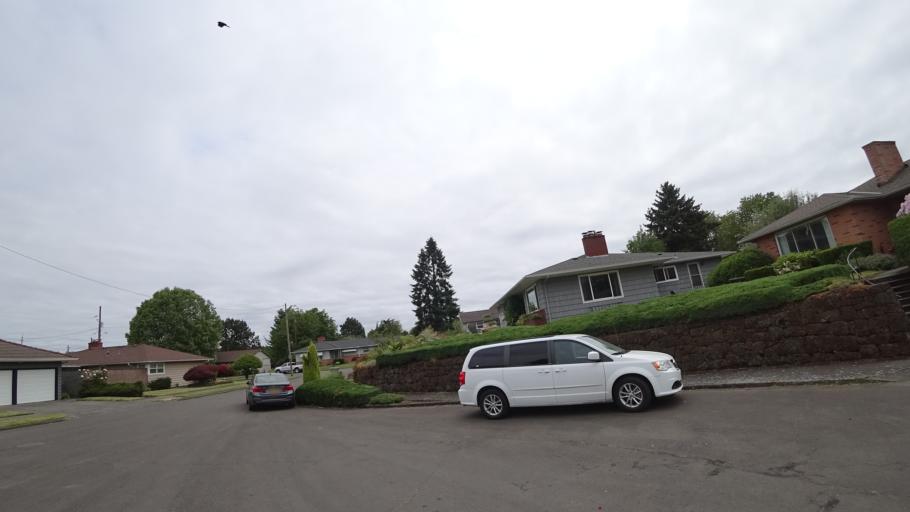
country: US
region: Oregon
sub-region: Multnomah County
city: Portland
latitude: 45.5709
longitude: -122.6323
